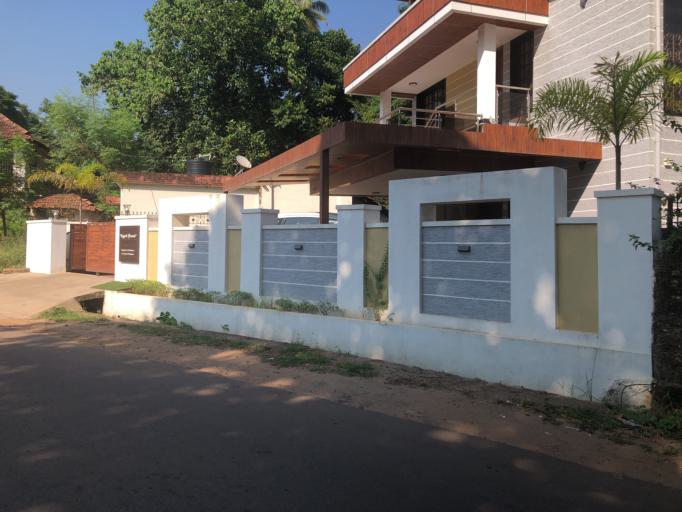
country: IN
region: Karnataka
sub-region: Dakshina Kannada
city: Mangalore
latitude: 12.8874
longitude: 74.8318
